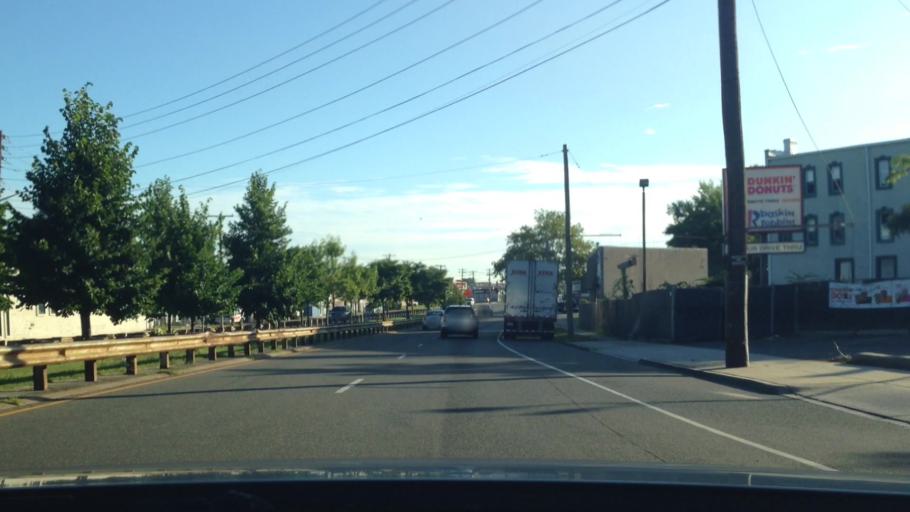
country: US
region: New York
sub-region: Nassau County
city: Hempstead
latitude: 40.6981
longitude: -73.6291
